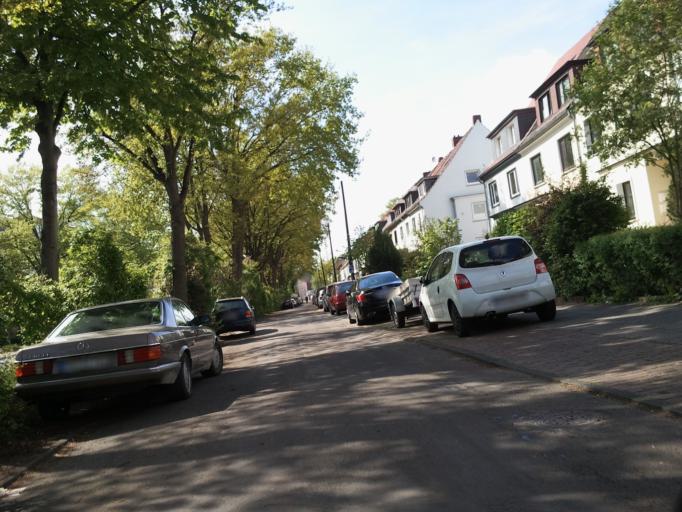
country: DE
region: Bremen
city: Bremen
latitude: 53.0761
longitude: 8.8418
